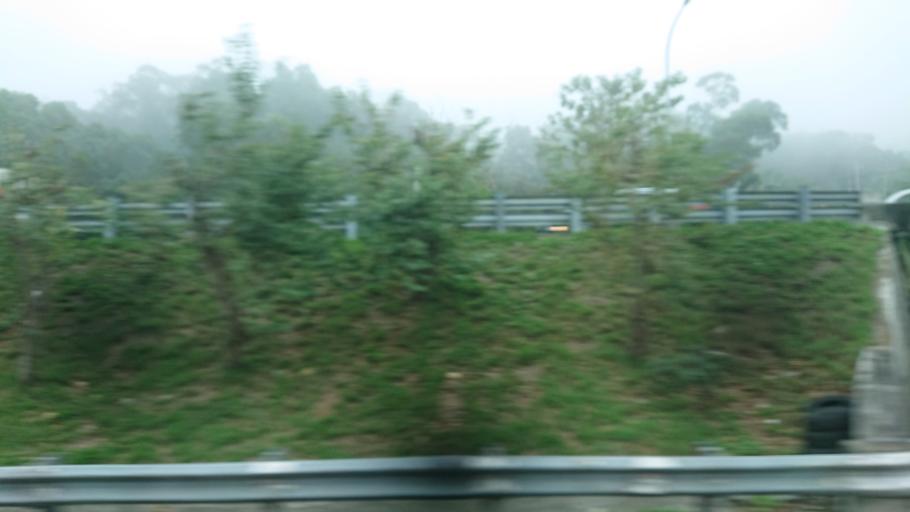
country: TW
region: Taiwan
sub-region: Miaoli
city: Miaoli
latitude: 24.4494
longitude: 120.7823
